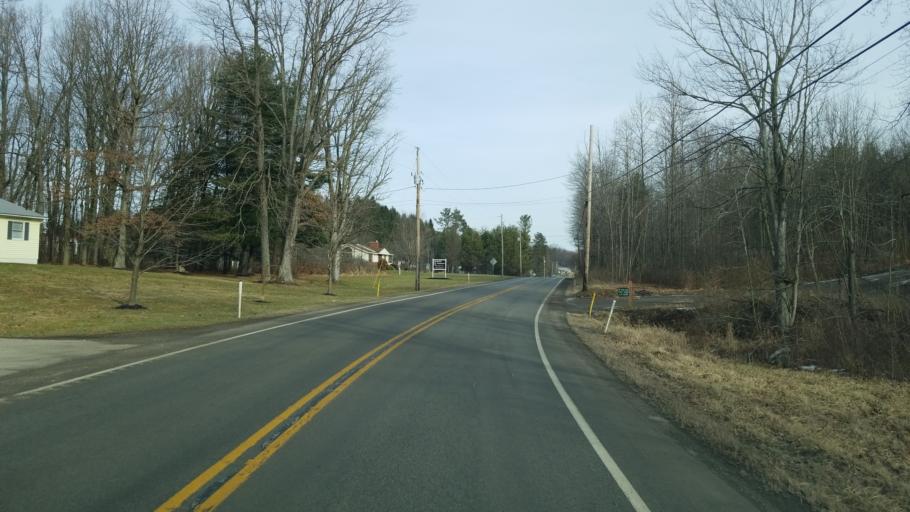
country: US
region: Pennsylvania
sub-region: Indiana County
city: Clymer
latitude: 40.7443
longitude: -78.8968
